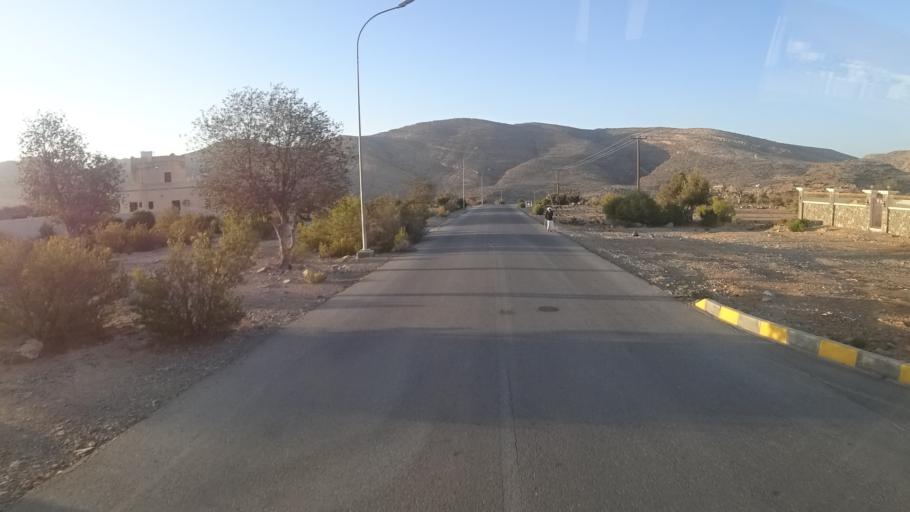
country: OM
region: Al Batinah
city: Bayt al `Awabi
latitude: 23.1441
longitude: 57.5390
